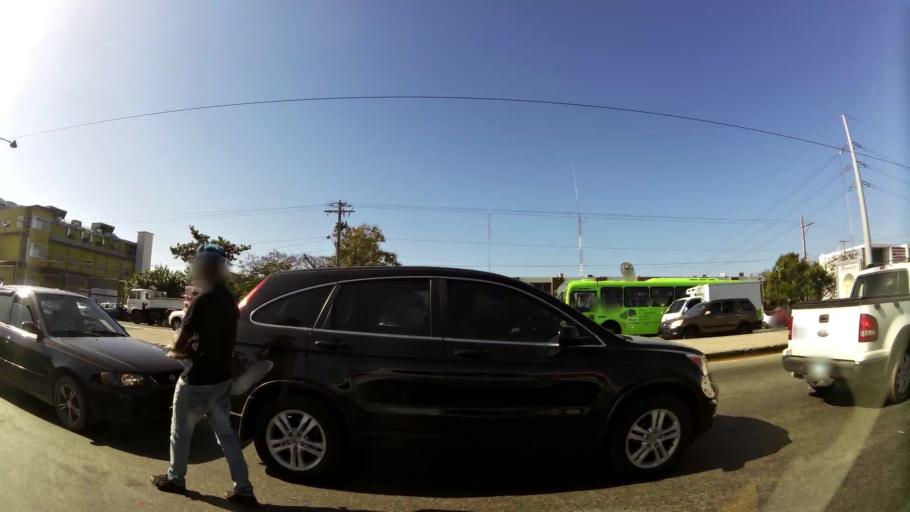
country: DO
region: Nacional
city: Bella Vista
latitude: 18.4508
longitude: -69.9776
